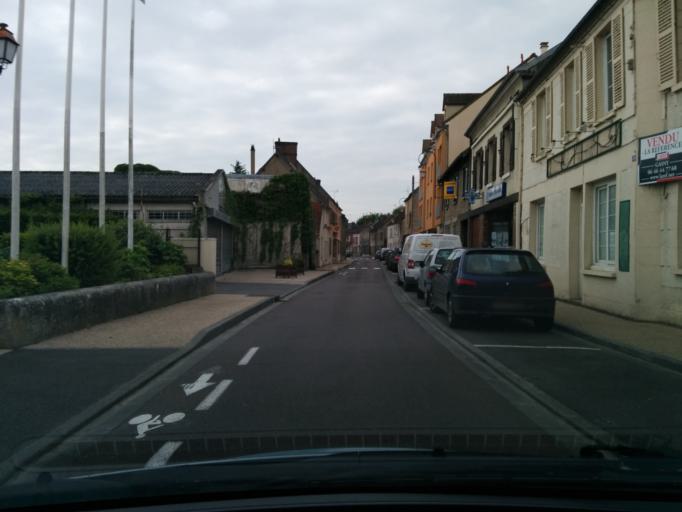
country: FR
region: Haute-Normandie
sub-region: Departement de l'Eure
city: Gasny
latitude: 49.0914
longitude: 1.6049
